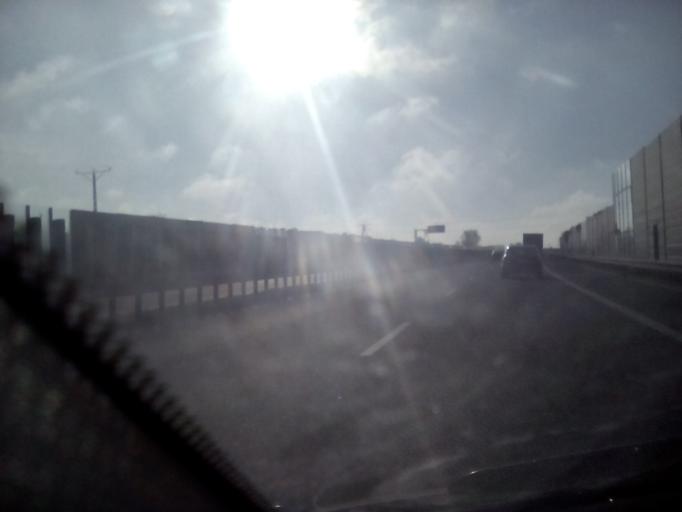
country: PL
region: Masovian Voivodeship
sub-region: Powiat grojecki
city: Grojec
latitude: 51.8541
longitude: 20.8662
